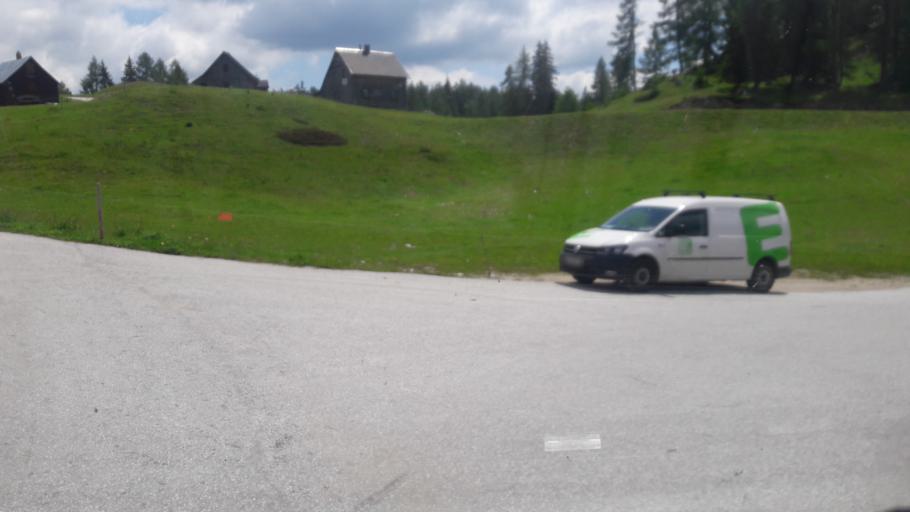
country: AT
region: Styria
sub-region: Politischer Bezirk Liezen
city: Tauplitz
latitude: 47.5932
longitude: 13.9862
